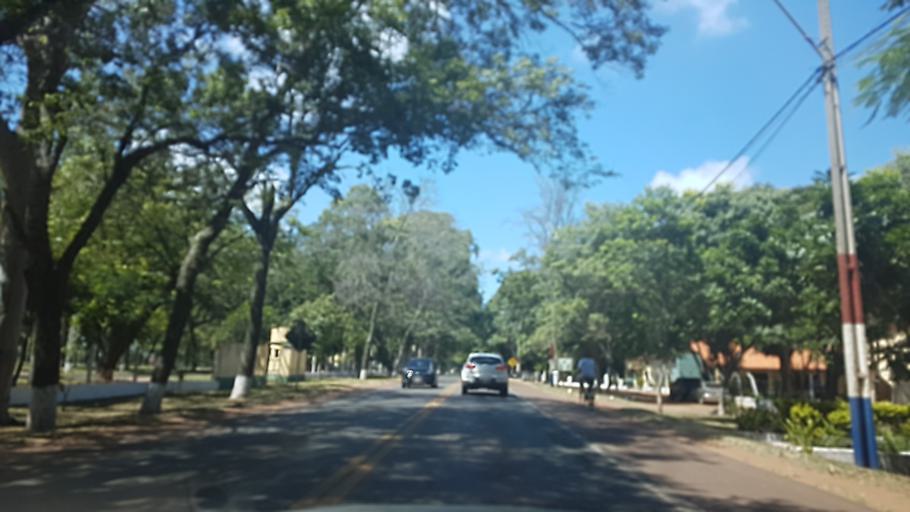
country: PY
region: Misiones
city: San Juan Bautista
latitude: -26.6679
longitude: -57.1339
